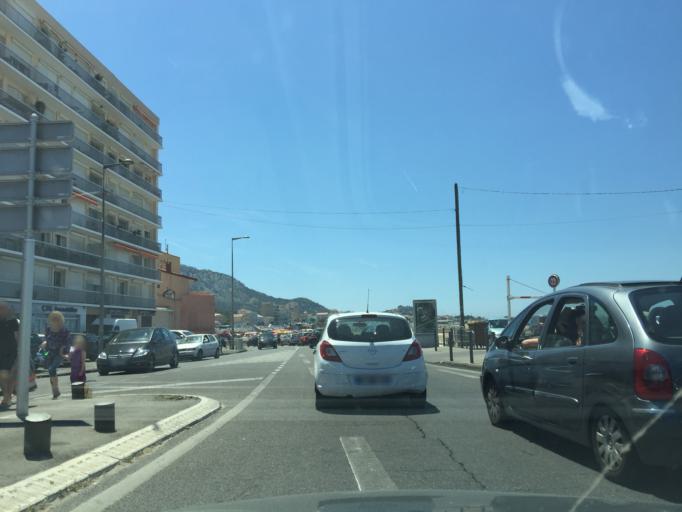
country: FR
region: Provence-Alpes-Cote d'Azur
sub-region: Departement des Bouches-du-Rhone
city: Marseille 08
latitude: 43.2478
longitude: 5.3744
